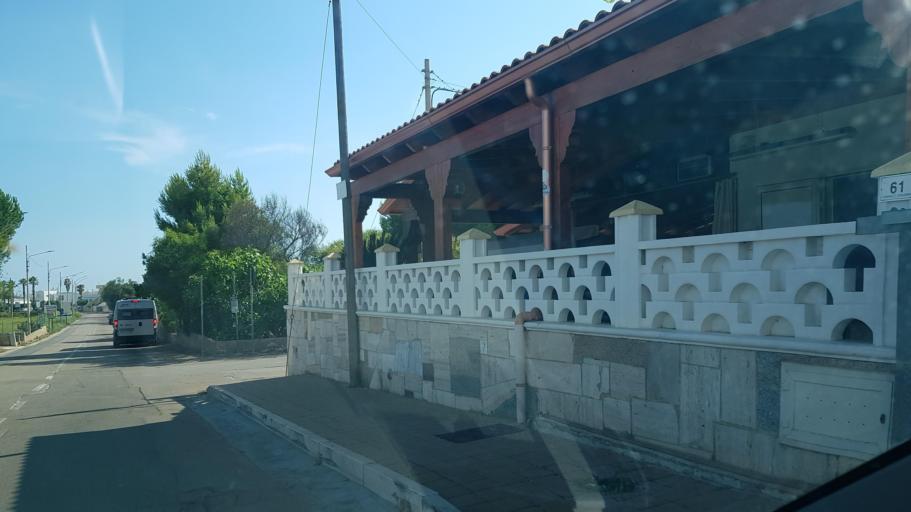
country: IT
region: Apulia
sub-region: Provincia di Lecce
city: Gemini
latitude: 39.8432
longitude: 18.2097
